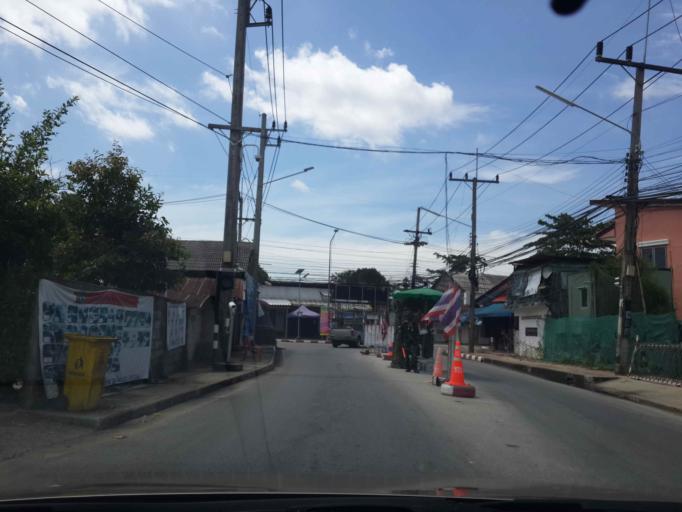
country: TH
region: Narathiwat
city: Rueso
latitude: 6.3989
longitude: 101.5206
